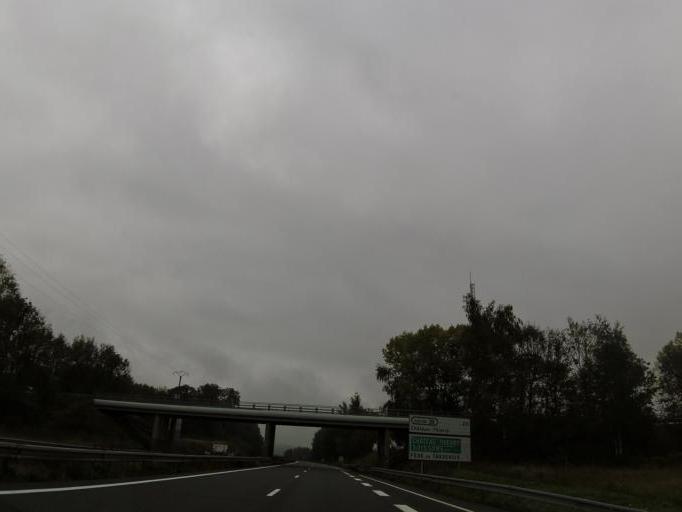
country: FR
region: Picardie
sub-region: Departement de l'Aisne
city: Montreuil-aux-Lions
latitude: 49.0151
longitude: 3.1549
